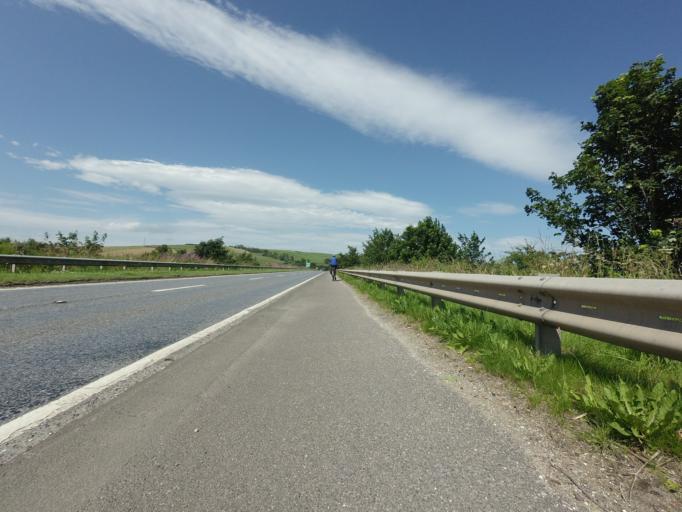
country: GB
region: Scotland
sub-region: Highland
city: Conon Bridge
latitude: 57.5748
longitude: -4.4317
